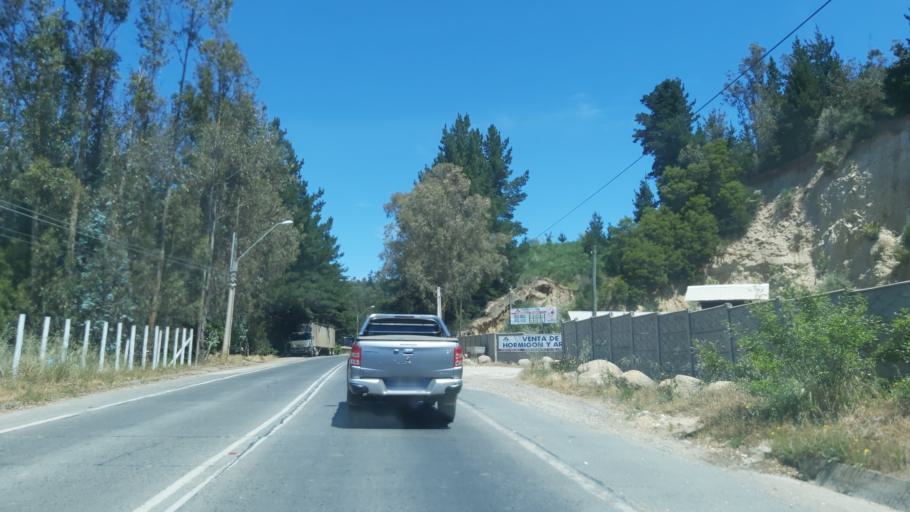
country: CL
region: Maule
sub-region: Provincia de Talca
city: Constitucion
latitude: -35.3485
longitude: -72.4136
